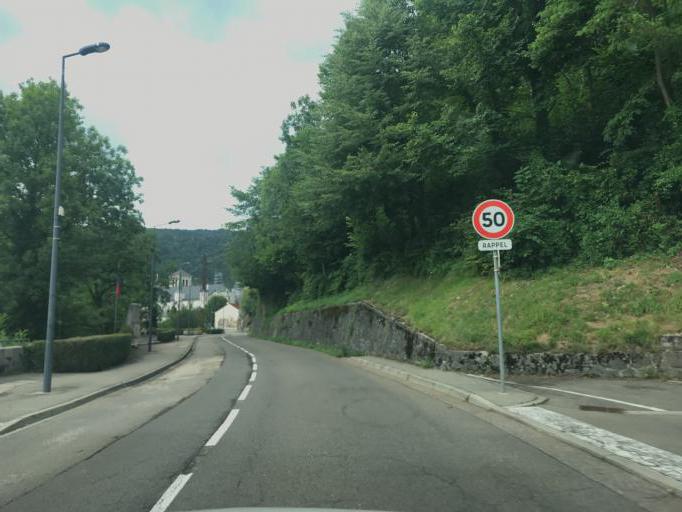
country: FR
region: Franche-Comte
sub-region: Departement du Jura
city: Saint-Claude
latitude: 46.3842
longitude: 5.8700
